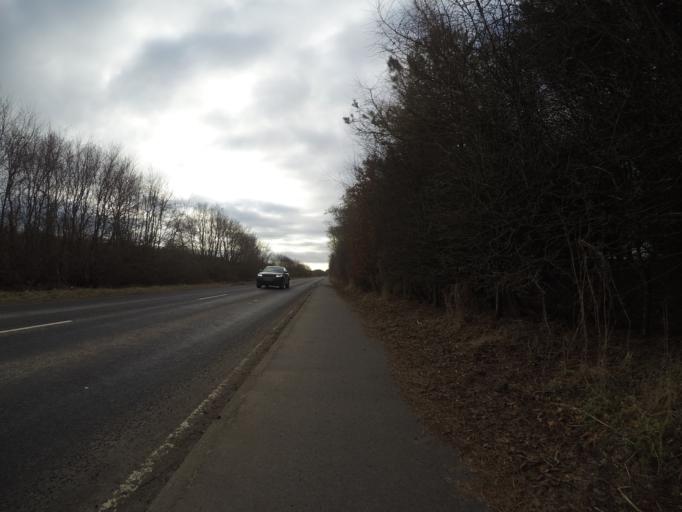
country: GB
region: Scotland
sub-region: North Ayrshire
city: Irvine
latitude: 55.5896
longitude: -4.6503
